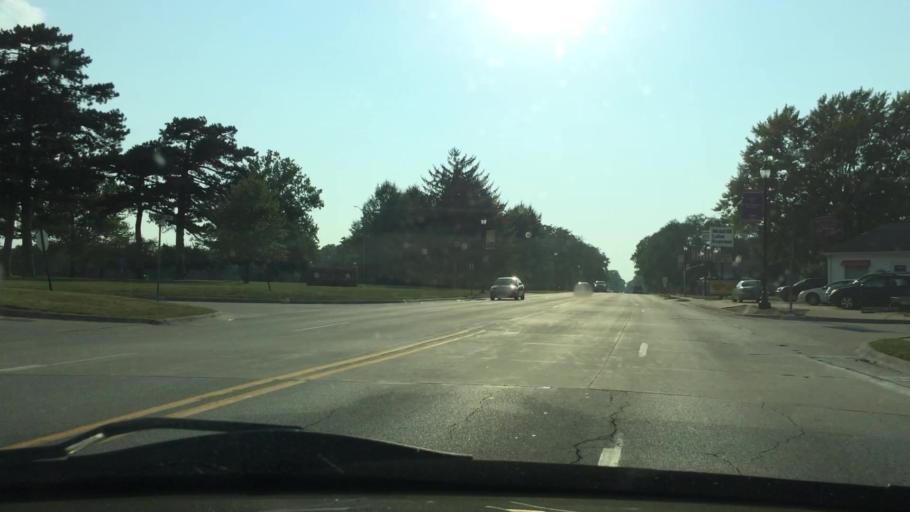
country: US
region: Iowa
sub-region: Henry County
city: Mount Pleasant
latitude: 40.9636
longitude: -91.5348
